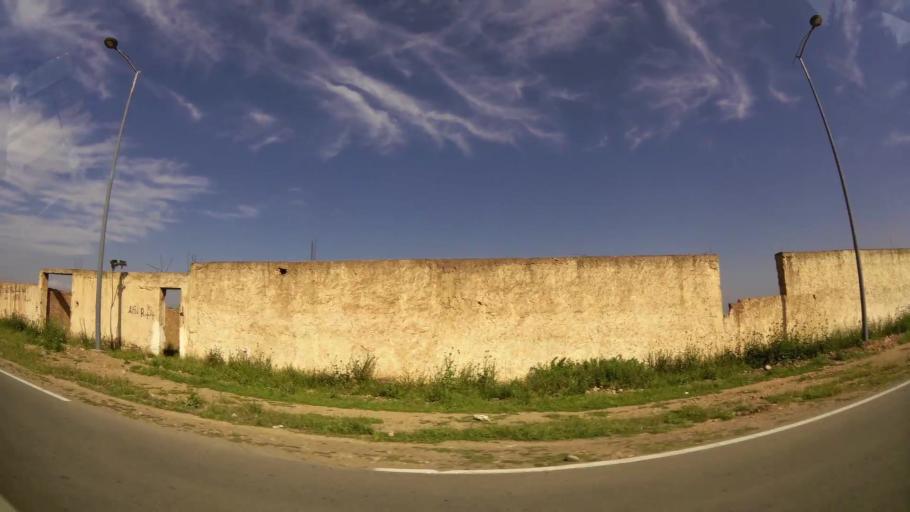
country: MA
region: Oriental
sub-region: Oujda-Angad
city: Oujda
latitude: 34.7225
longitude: -1.8795
